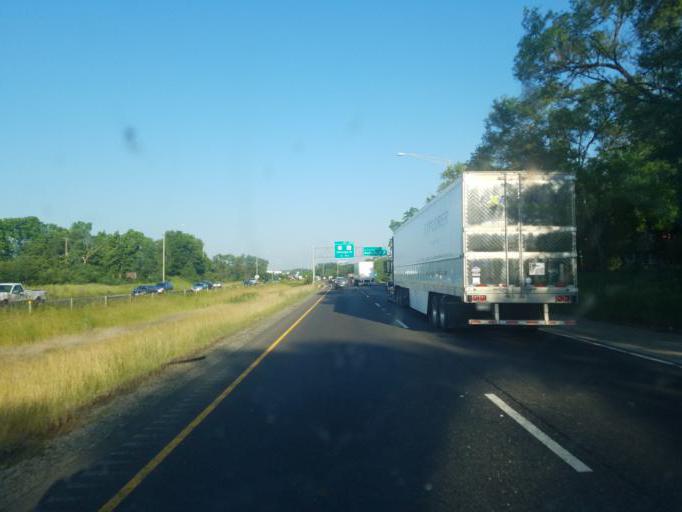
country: US
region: Illinois
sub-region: Will County
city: Joliet
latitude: 41.5133
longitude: -88.0687
